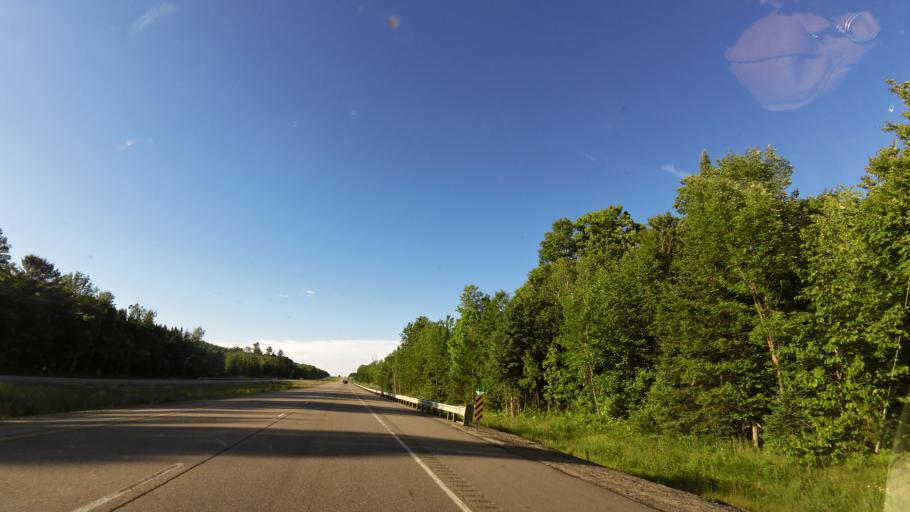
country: CA
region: Ontario
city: Orillia
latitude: 44.6398
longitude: -79.6532
